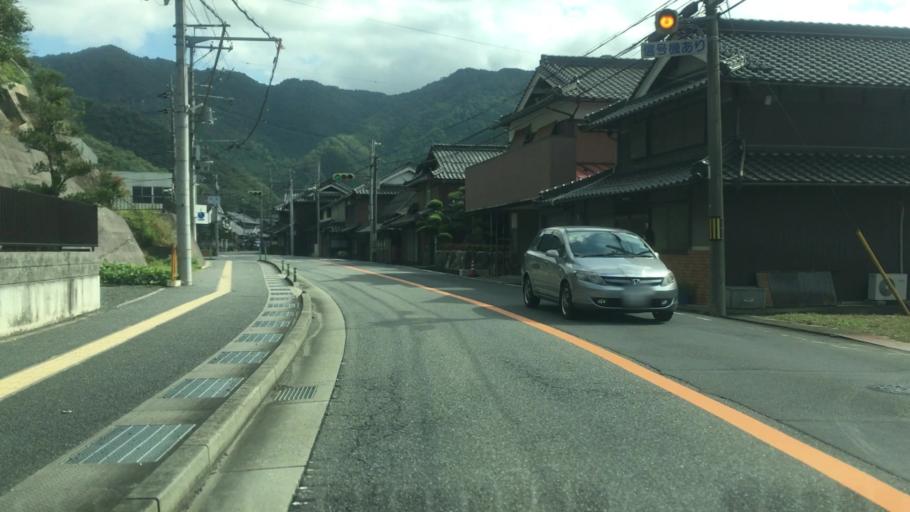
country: JP
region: Kyoto
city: Fukuchiyama
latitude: 35.1497
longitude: 135.0598
